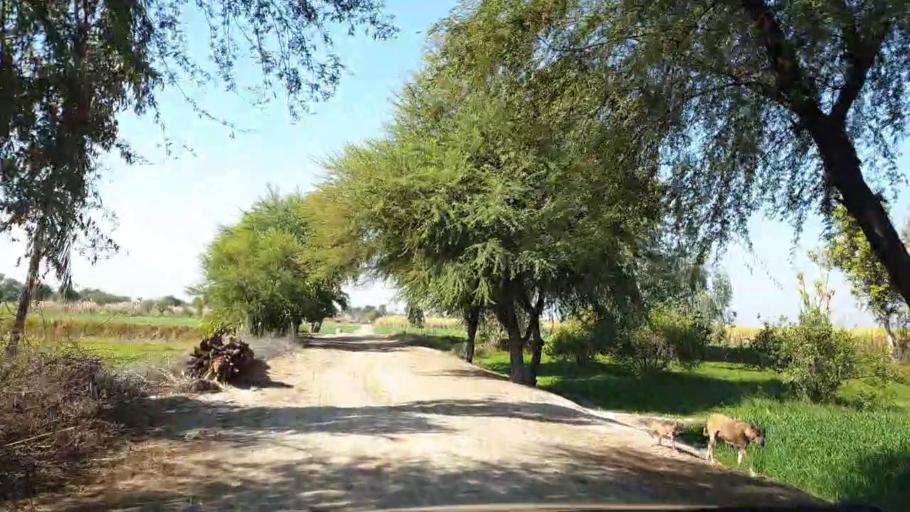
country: PK
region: Sindh
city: Sinjhoro
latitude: 26.1109
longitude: 68.8379
